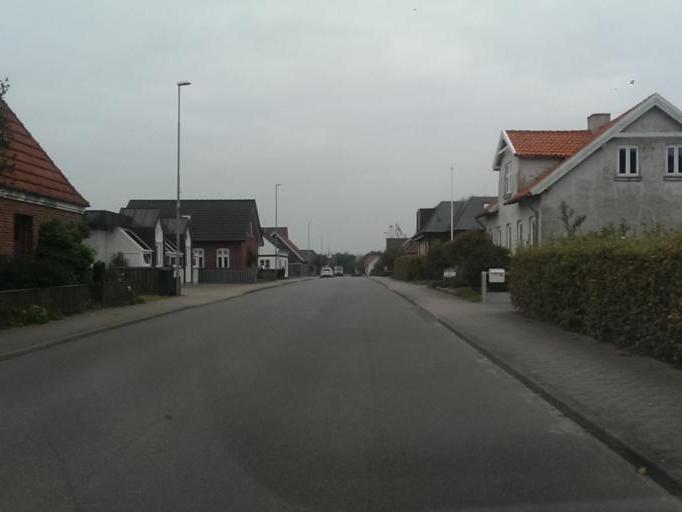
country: DK
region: South Denmark
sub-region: Esbjerg Kommune
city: Tjaereborg
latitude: 55.4646
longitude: 8.5762
